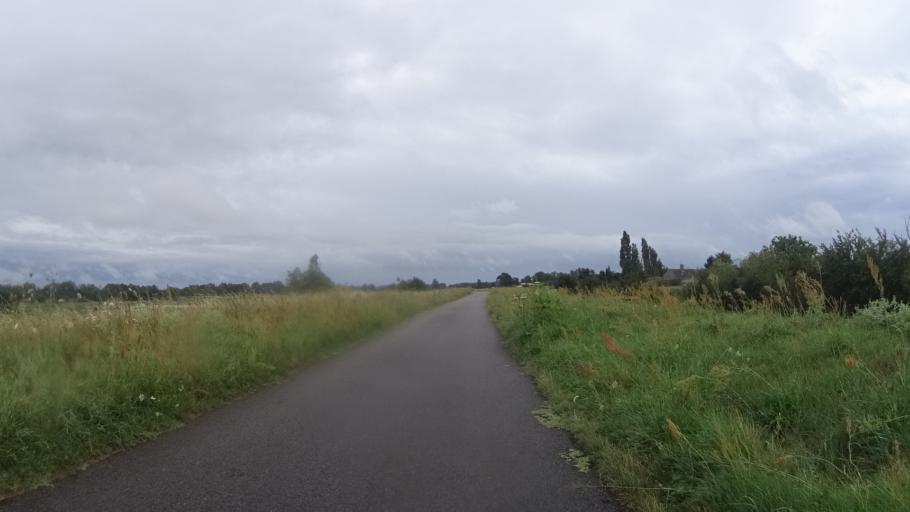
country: FR
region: Centre
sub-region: Departement du Loiret
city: Checy
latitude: 47.8817
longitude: 2.0157
